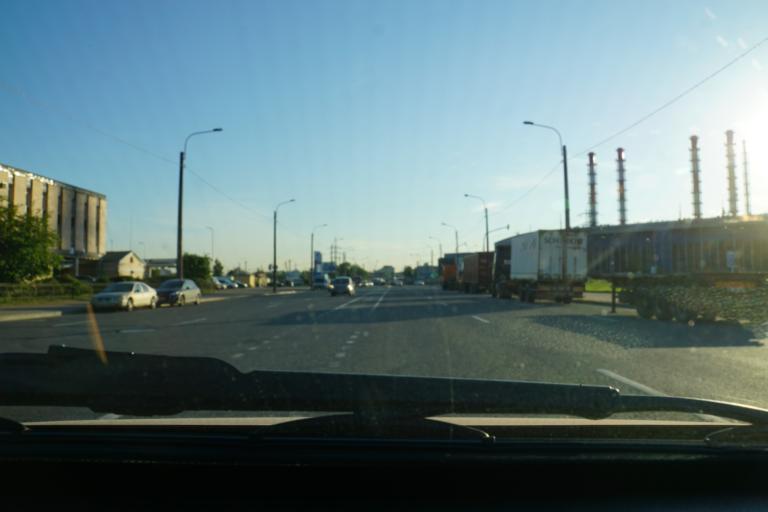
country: RU
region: St.-Petersburg
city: Avtovo
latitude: 59.8670
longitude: 30.2512
